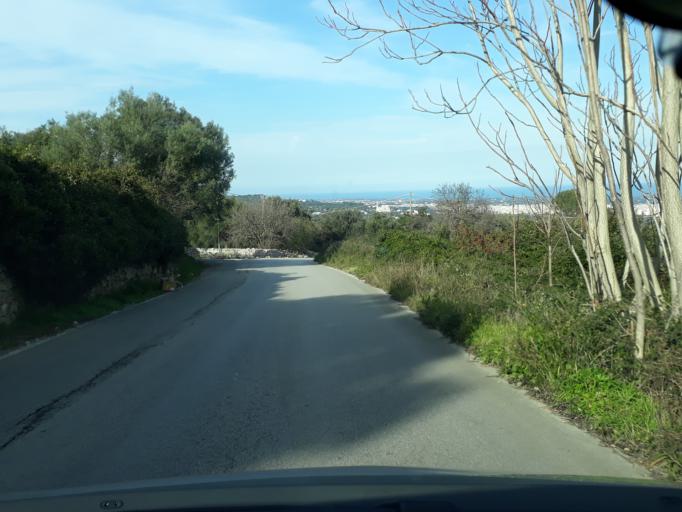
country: IT
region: Apulia
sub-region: Provincia di Brindisi
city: Lamie di Olimpie-Selva
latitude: 40.8054
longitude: 17.3523
